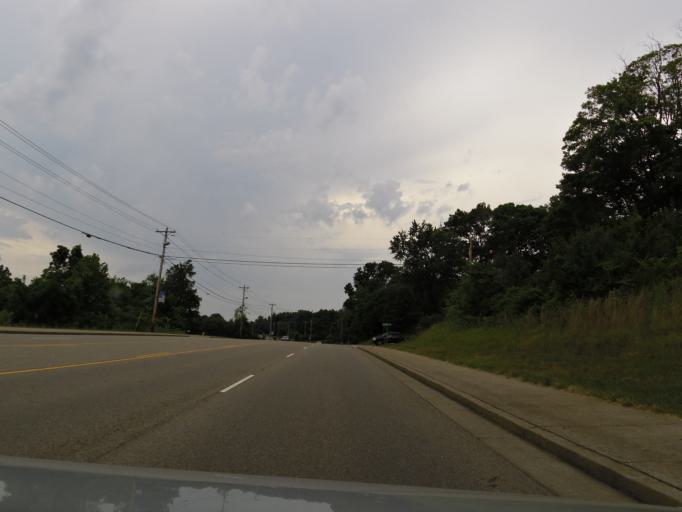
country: US
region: Tennessee
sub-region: Knox County
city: Farragut
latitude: 35.8735
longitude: -84.1471
